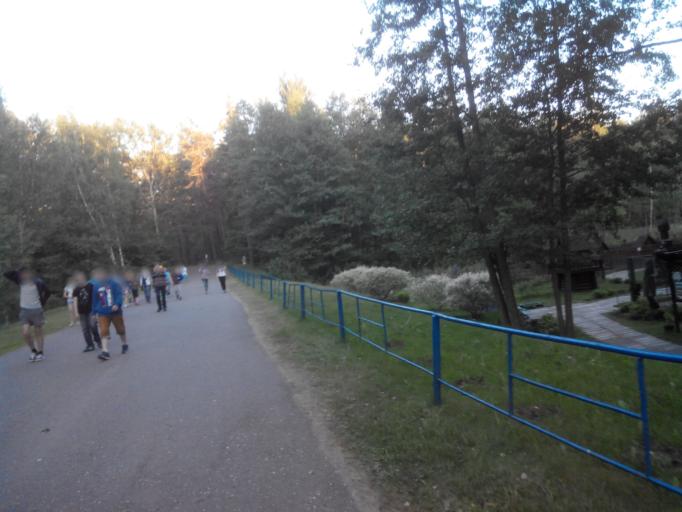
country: BY
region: Minsk
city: Narach
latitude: 54.8374
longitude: 26.7095
